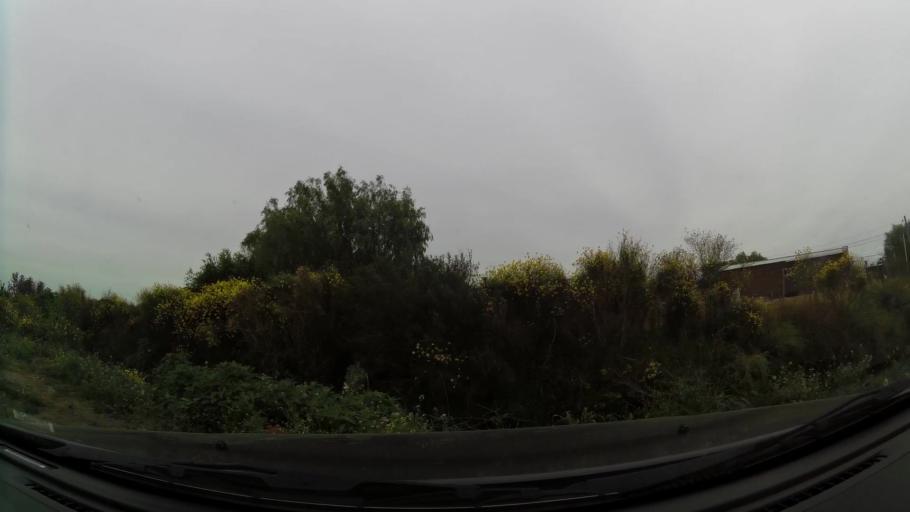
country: UY
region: Canelones
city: Las Piedras
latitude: -34.7330
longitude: -56.2044
